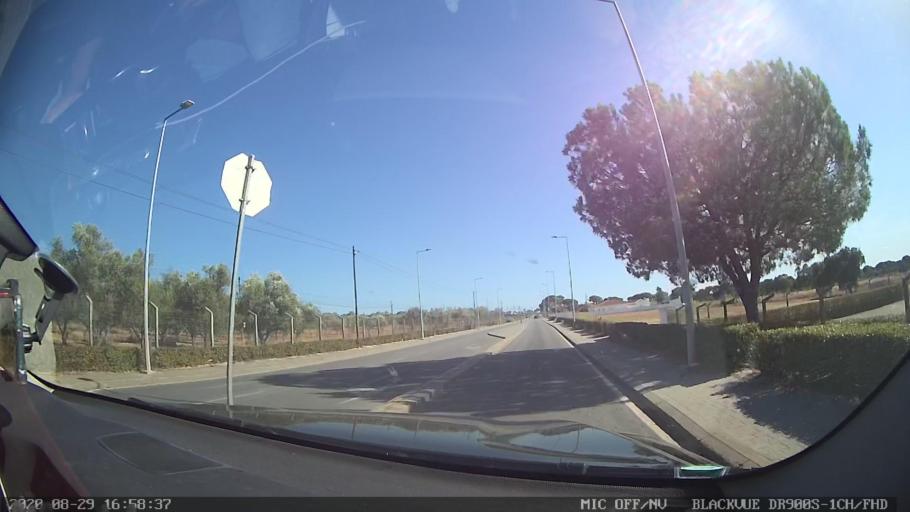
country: PT
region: Setubal
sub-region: Alcacer do Sal
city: Alcacer do Sal
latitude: 38.3946
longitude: -8.5141
